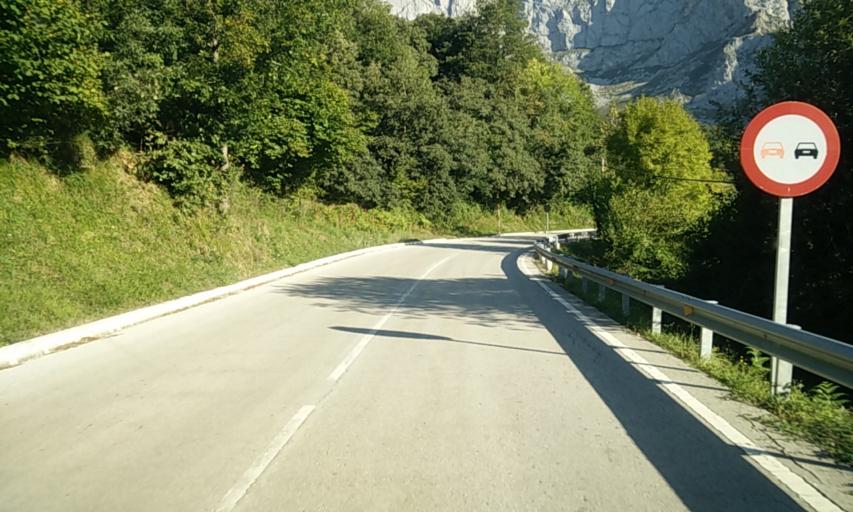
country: ES
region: Castille and Leon
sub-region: Provincia de Leon
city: Posada de Valdeon
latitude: 43.1374
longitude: -4.8108
